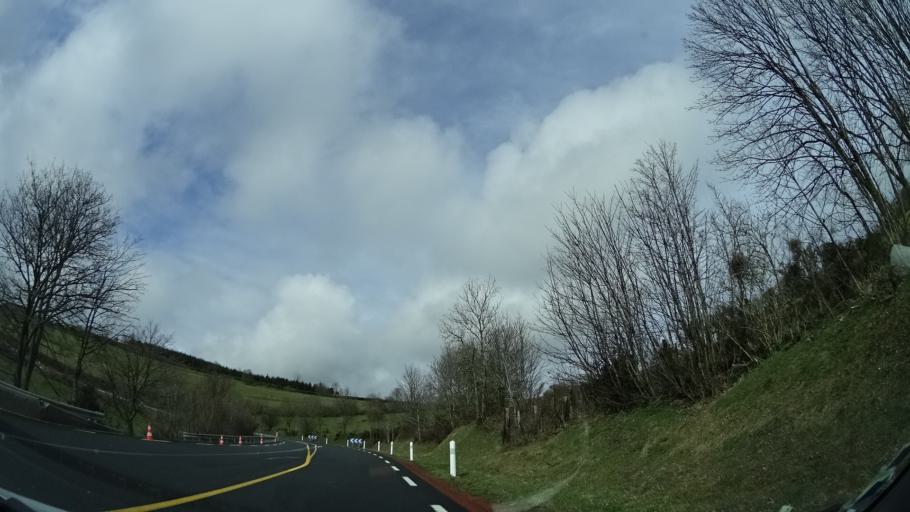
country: FR
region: Rhone-Alpes
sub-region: Departement de la Loire
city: Violay
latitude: 45.9126
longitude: 4.3572
